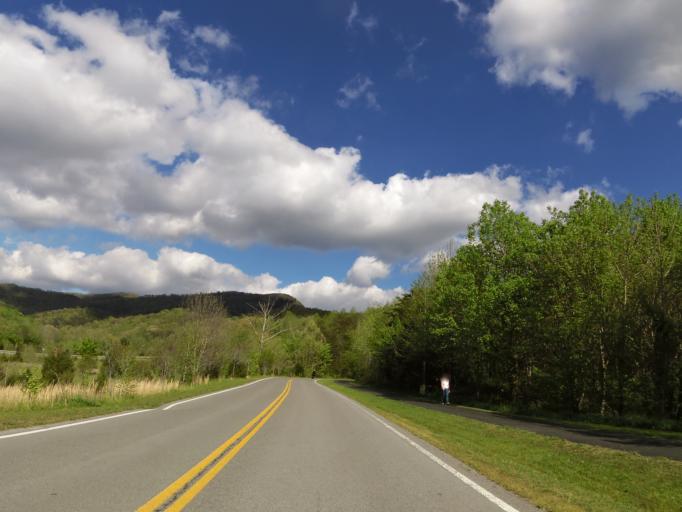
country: US
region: Kentucky
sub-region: Bell County
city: Middlesboro
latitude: 36.6042
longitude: -83.6947
